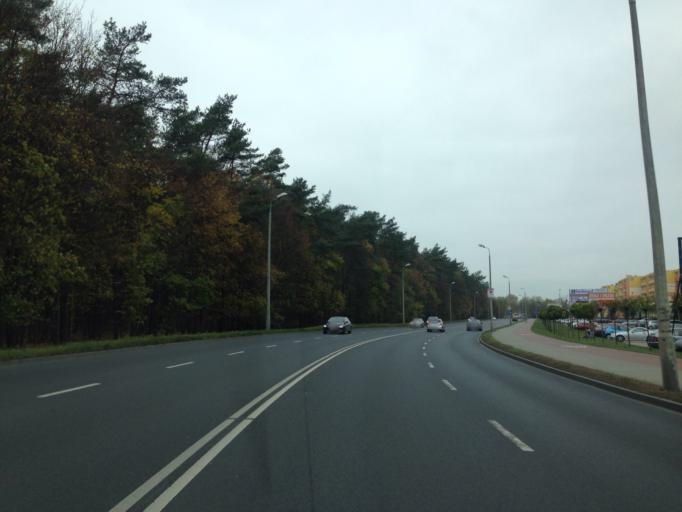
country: PL
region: Kujawsko-Pomorskie
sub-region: Grudziadz
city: Grudziadz
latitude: 53.4615
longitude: 18.7700
